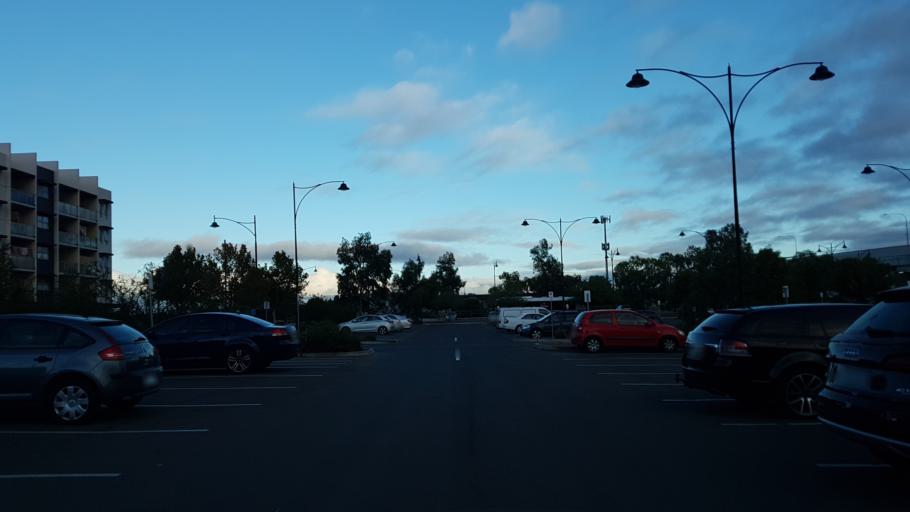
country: AU
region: South Australia
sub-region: Salisbury
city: Ingle Farm
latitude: -34.8053
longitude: 138.6142
